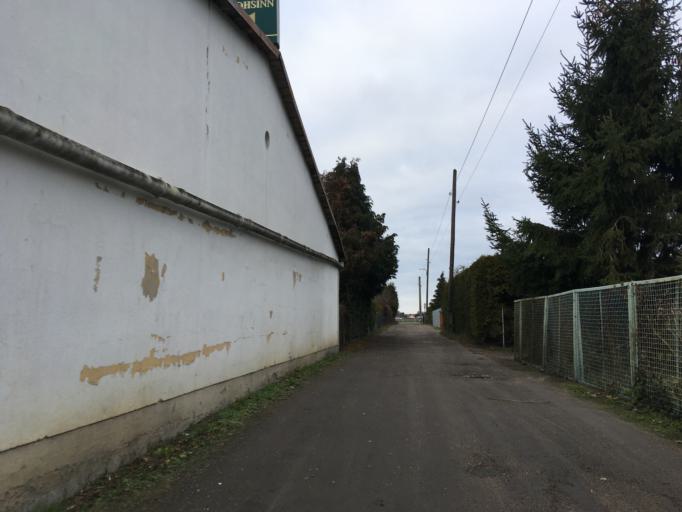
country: DE
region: Berlin
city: Buchholz
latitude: 52.6035
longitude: 13.4122
